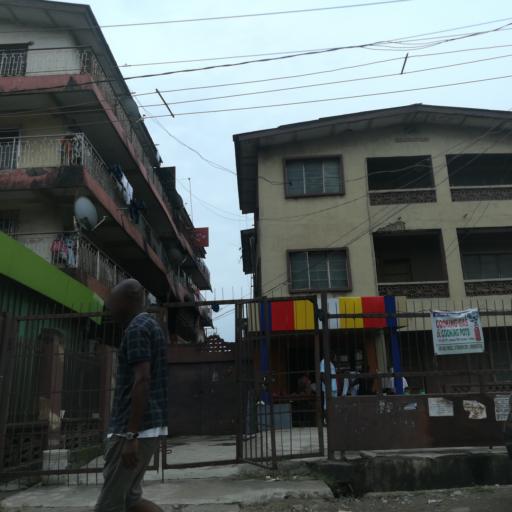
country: NG
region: Lagos
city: Makoko
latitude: 6.5081
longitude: 3.3873
